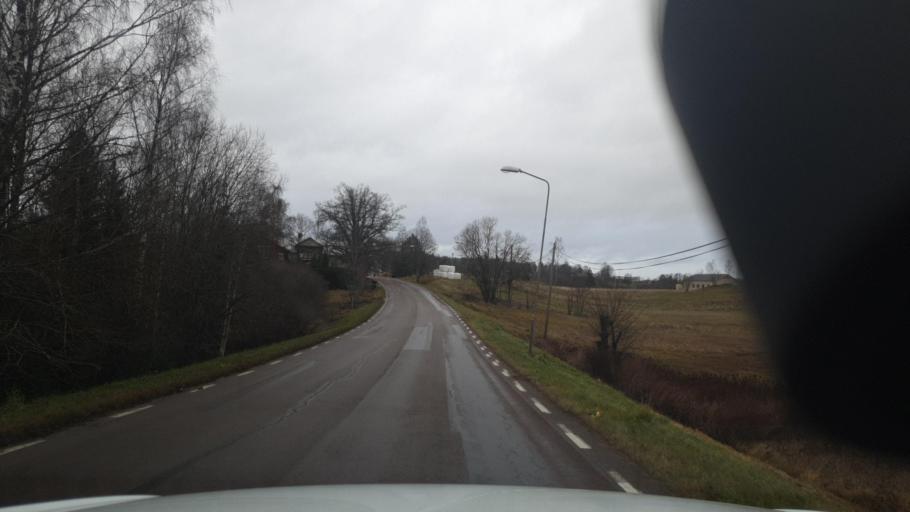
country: SE
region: Vaermland
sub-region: Karlstads Kommun
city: Edsvalla
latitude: 59.5522
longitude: 13.0532
